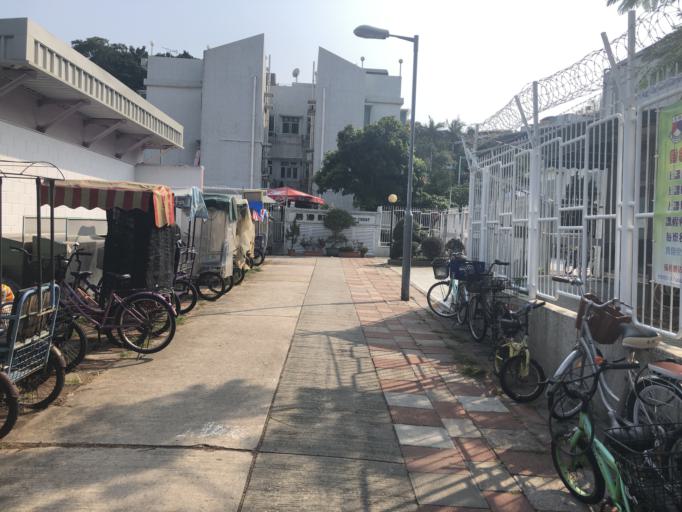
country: HK
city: Yung Shue Wan
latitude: 22.2048
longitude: 114.0243
